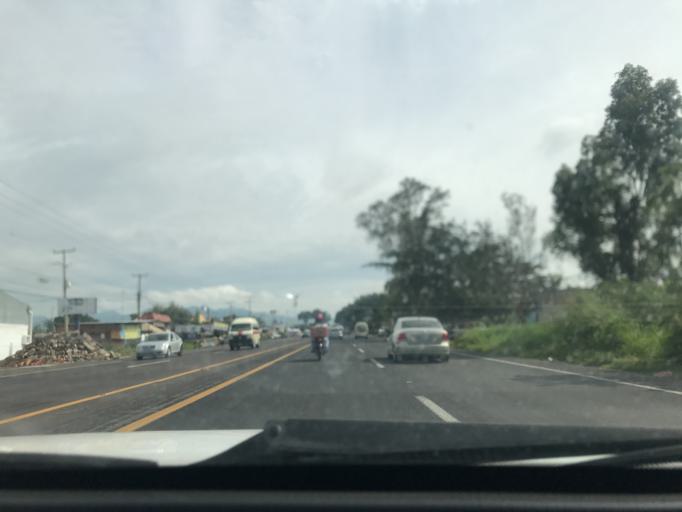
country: MX
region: Morelos
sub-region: Atlatlahucan
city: Colonia San Francisco
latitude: 18.8797
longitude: -98.9205
